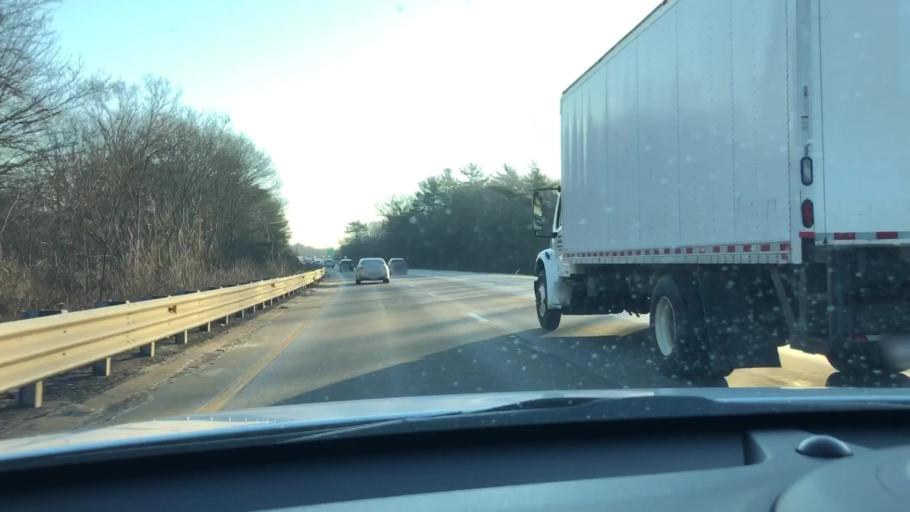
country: US
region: Massachusetts
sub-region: Norfolk County
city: Weymouth
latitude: 42.1884
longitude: -70.9395
